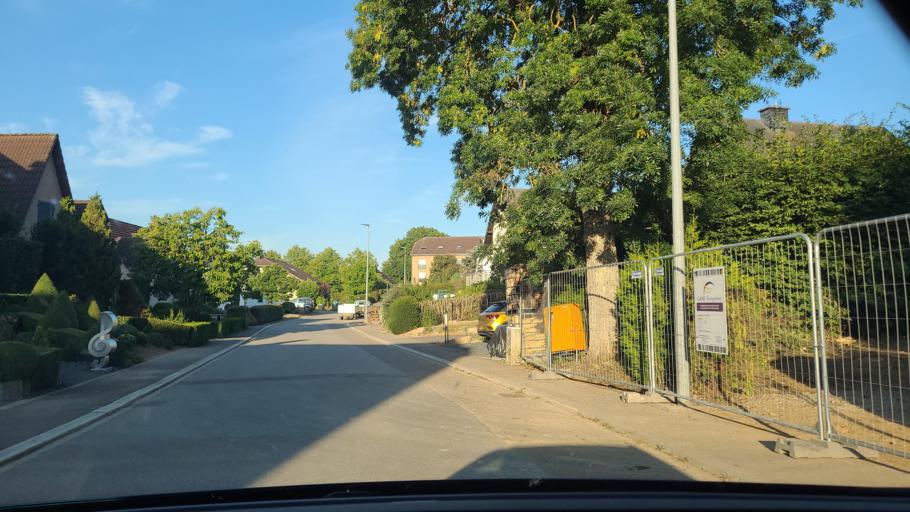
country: LU
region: Luxembourg
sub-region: Canton de Capellen
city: Garnich
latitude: 49.6141
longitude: 5.9533
